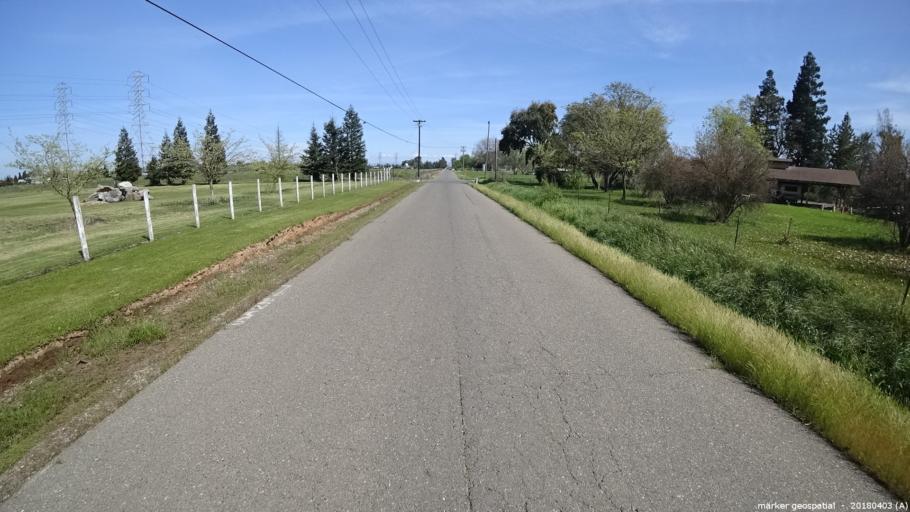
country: US
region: California
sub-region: Sacramento County
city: Clay
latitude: 38.3505
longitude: -121.2154
